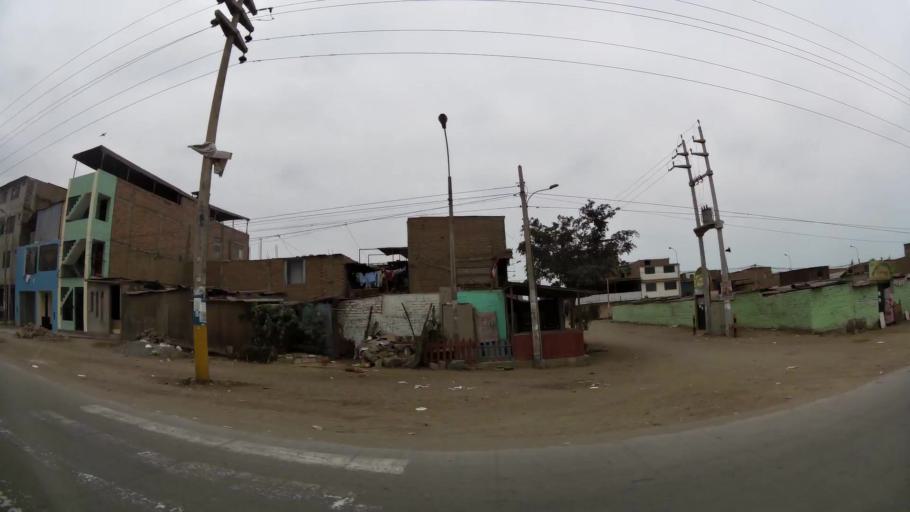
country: PE
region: Lima
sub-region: Lima
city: Surco
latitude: -12.2050
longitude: -76.9514
